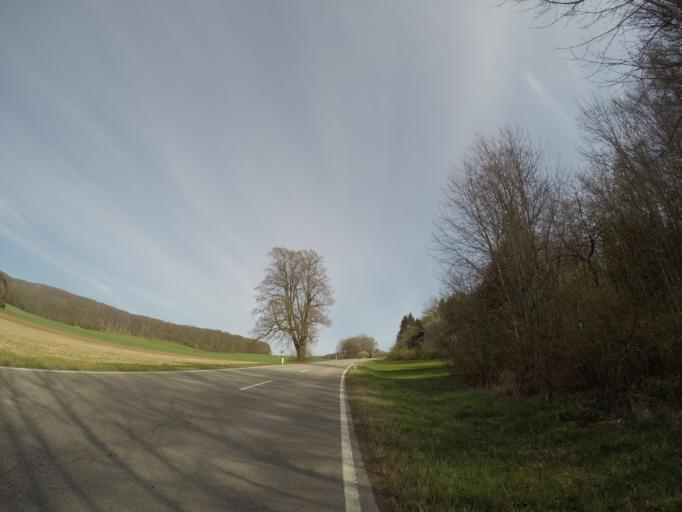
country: DE
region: Baden-Wuerttemberg
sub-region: Regierungsbezirk Stuttgart
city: Hohenstadt
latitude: 48.5306
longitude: 9.6531
